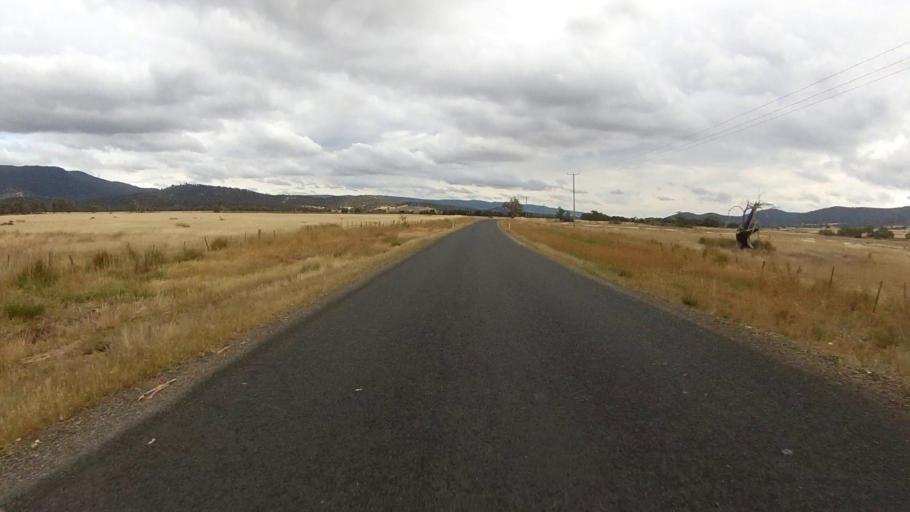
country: AU
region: Tasmania
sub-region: Break O'Day
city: St Helens
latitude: -41.8239
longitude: 147.8614
